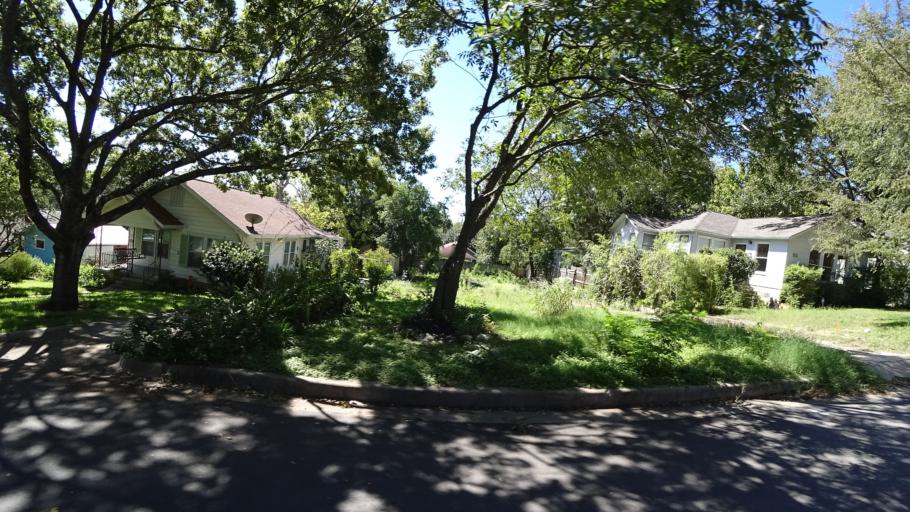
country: US
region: Texas
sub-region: Travis County
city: Austin
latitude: 30.2423
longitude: -97.7473
